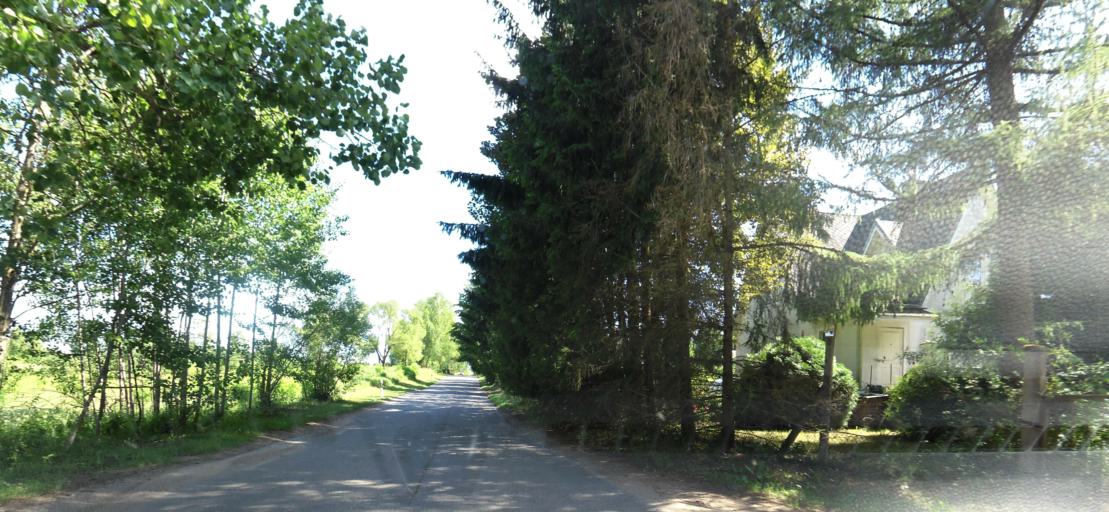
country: LT
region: Vilnius County
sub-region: Vilnius
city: Fabijoniskes
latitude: 54.8133
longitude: 25.3221
